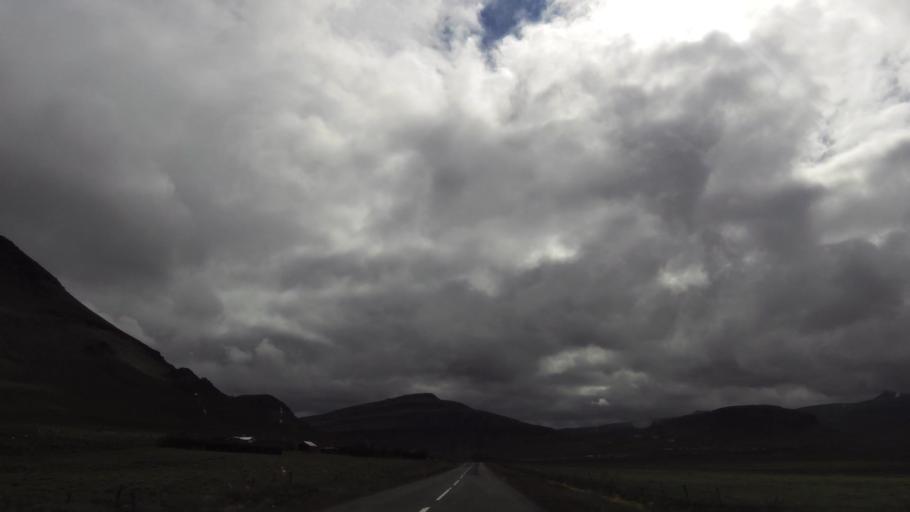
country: IS
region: West
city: Borgarnes
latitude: 65.3906
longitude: -21.8821
